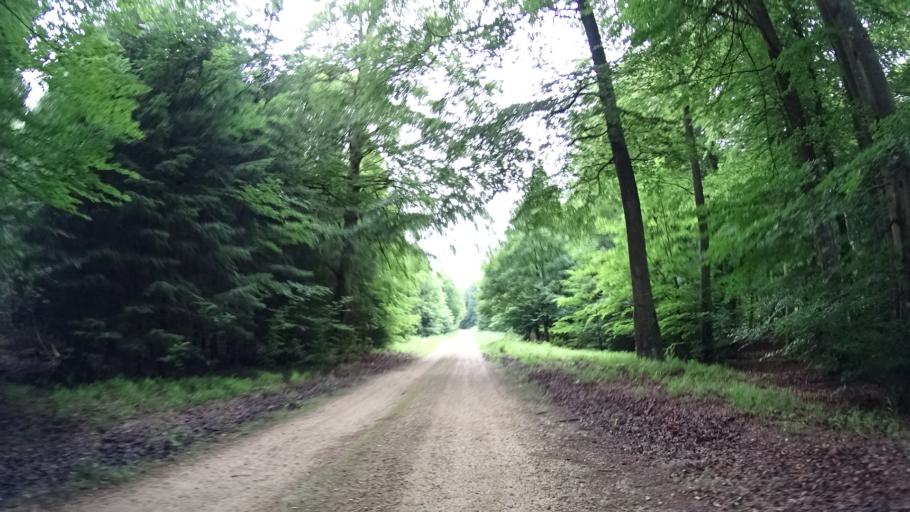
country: DE
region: Bavaria
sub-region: Upper Bavaria
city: Stammham
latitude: 48.8882
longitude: 11.5265
